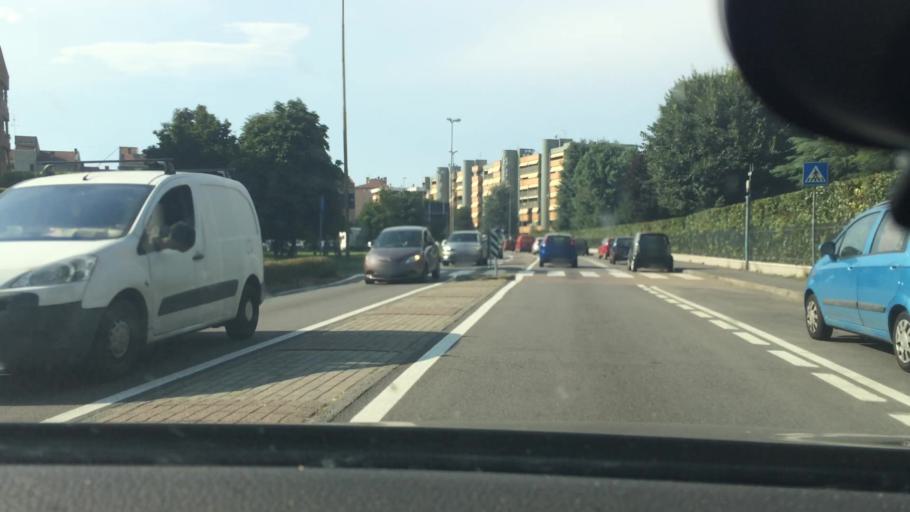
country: IT
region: Lombardy
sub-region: Citta metropolitana di Milano
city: Settimo Milanese
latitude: 45.4788
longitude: 9.0603
